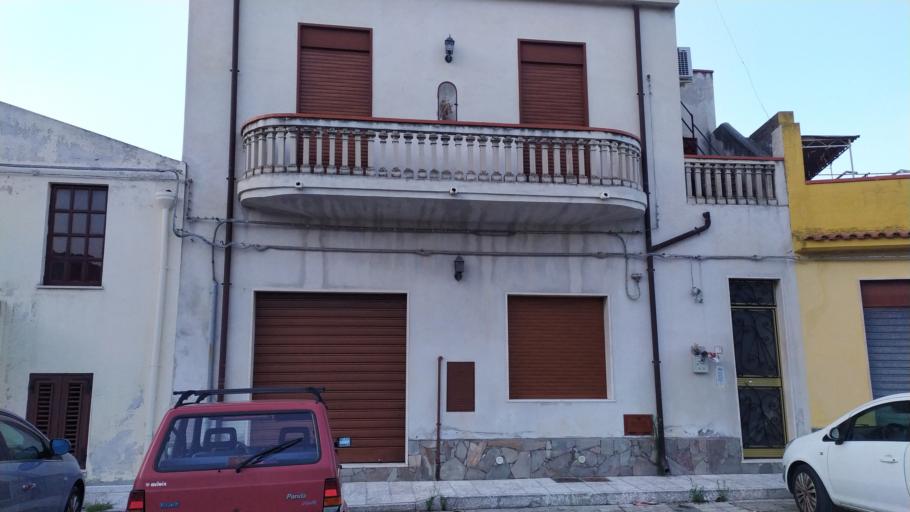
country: IT
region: Sicily
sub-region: Messina
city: Villafranca Tirrena
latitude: 38.2320
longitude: 15.4354
